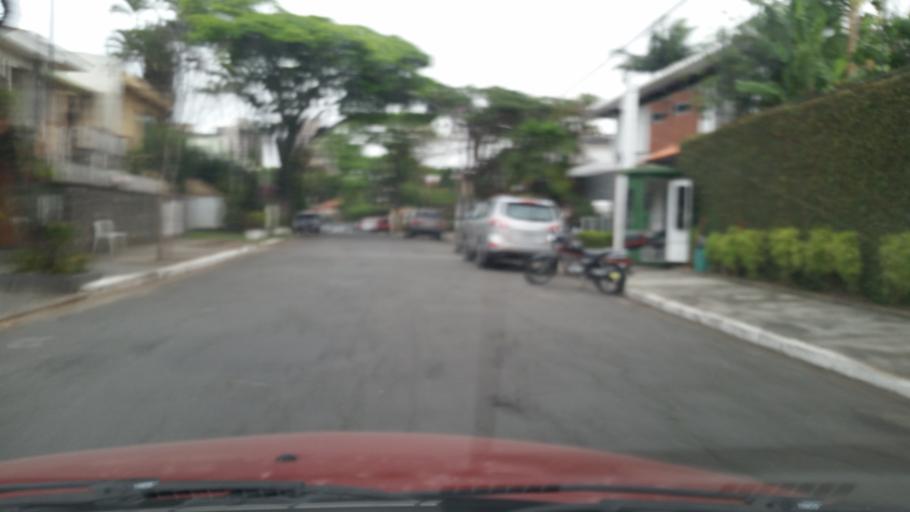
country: BR
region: Sao Paulo
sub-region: Diadema
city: Diadema
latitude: -23.6191
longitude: -46.6217
